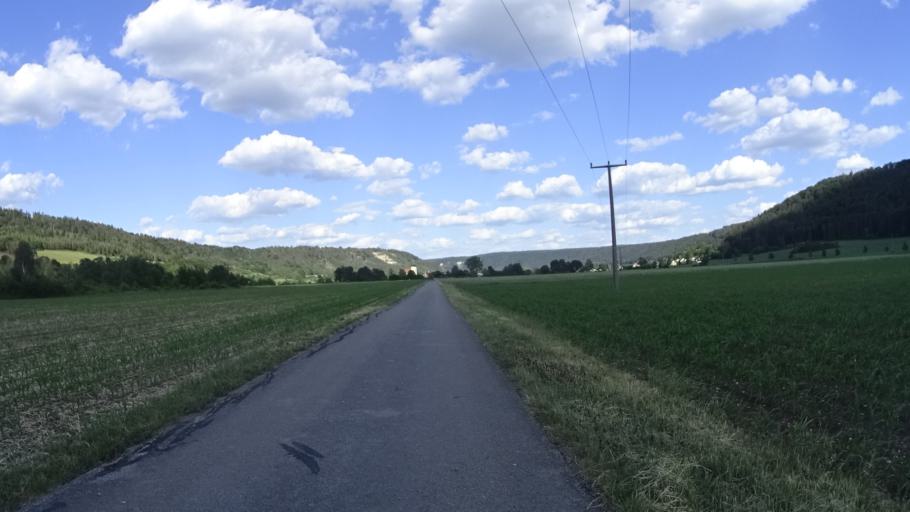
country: DE
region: Bavaria
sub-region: Upper Palatinate
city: Dietfurt
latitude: 49.0209
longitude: 11.5060
